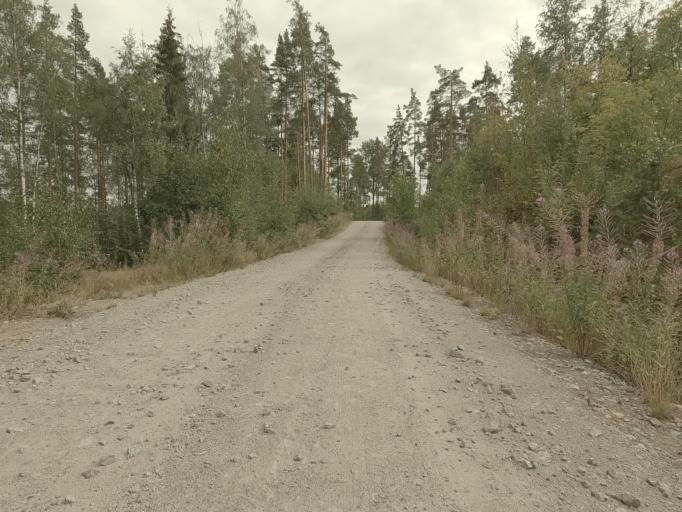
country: RU
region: Leningrad
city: Kamennogorsk
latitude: 60.9767
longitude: 29.1729
